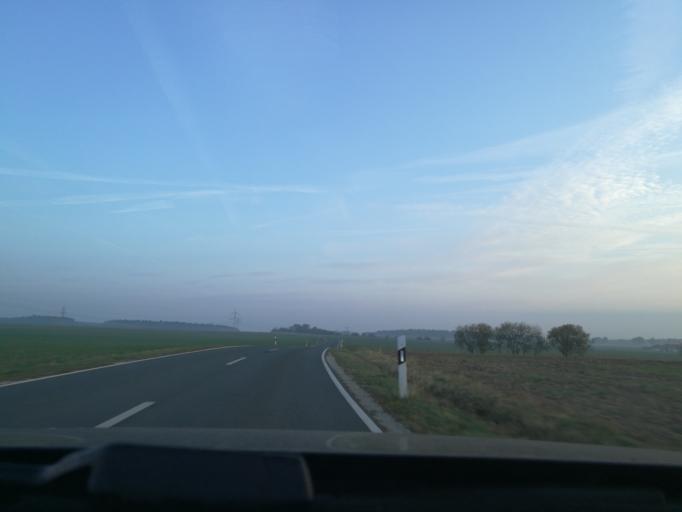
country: DE
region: Bavaria
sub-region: Regierungsbezirk Mittelfranken
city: Obermichelbach
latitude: 49.5346
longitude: 10.9097
